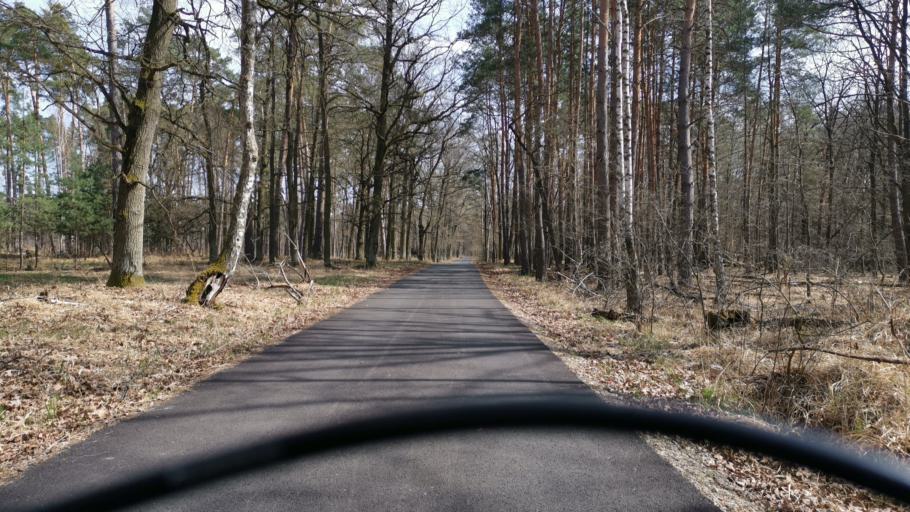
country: SK
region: Trnavsky
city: Gbely
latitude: 48.7107
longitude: 17.0651
